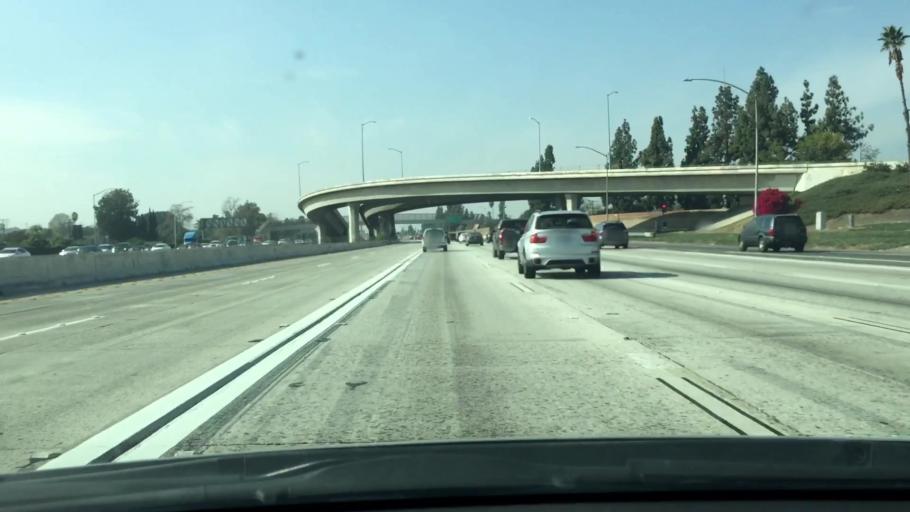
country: US
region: California
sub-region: Los Angeles County
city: South San Gabriel
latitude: 34.0723
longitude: -118.0999
